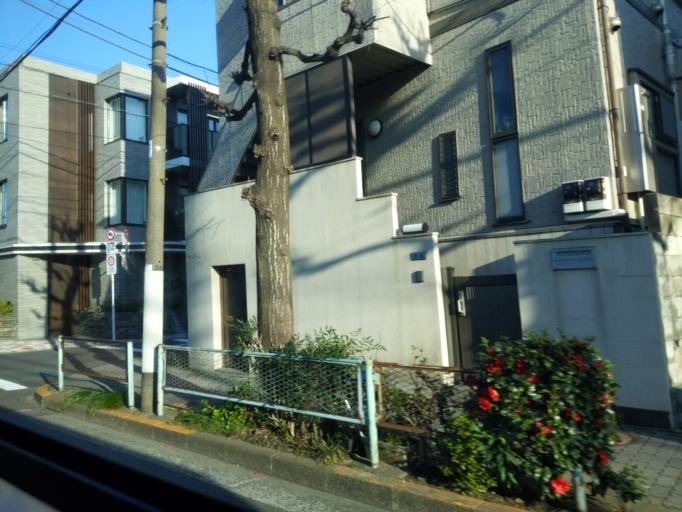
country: JP
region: Tokyo
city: Tokyo
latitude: 35.6329
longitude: 139.6948
